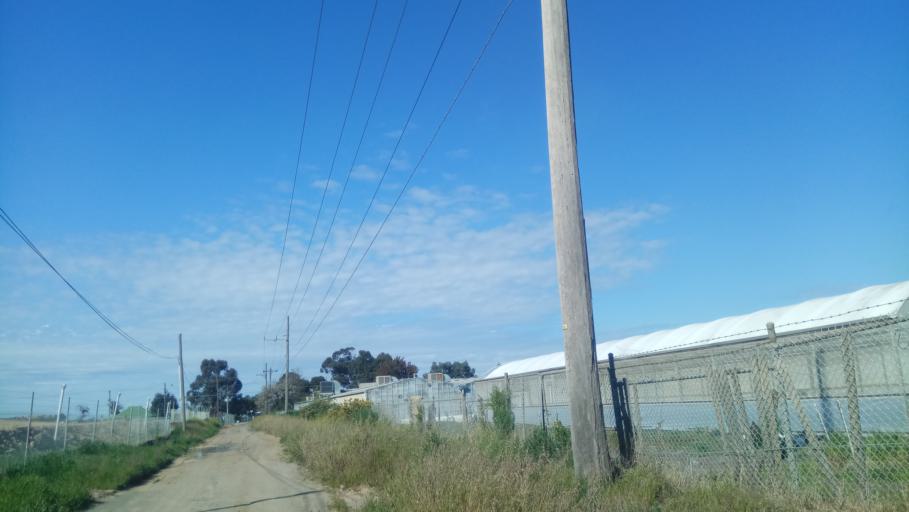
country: AU
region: Victoria
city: Heatherton
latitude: -37.9566
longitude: 145.1184
